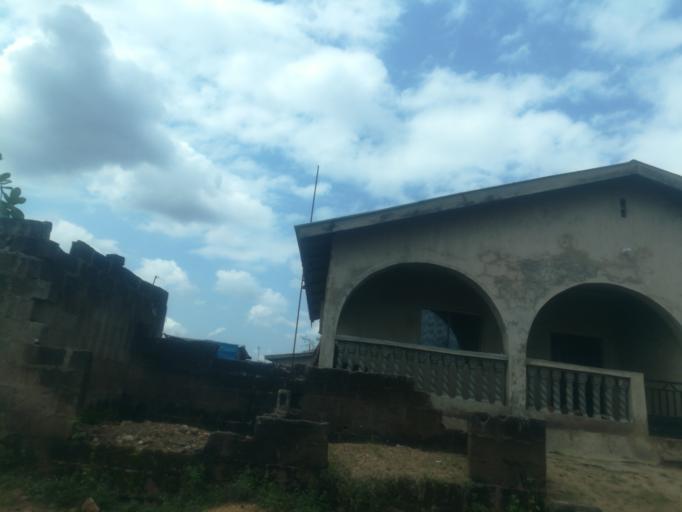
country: NG
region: Oyo
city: Egbeda
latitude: 7.4161
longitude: 4.0031
